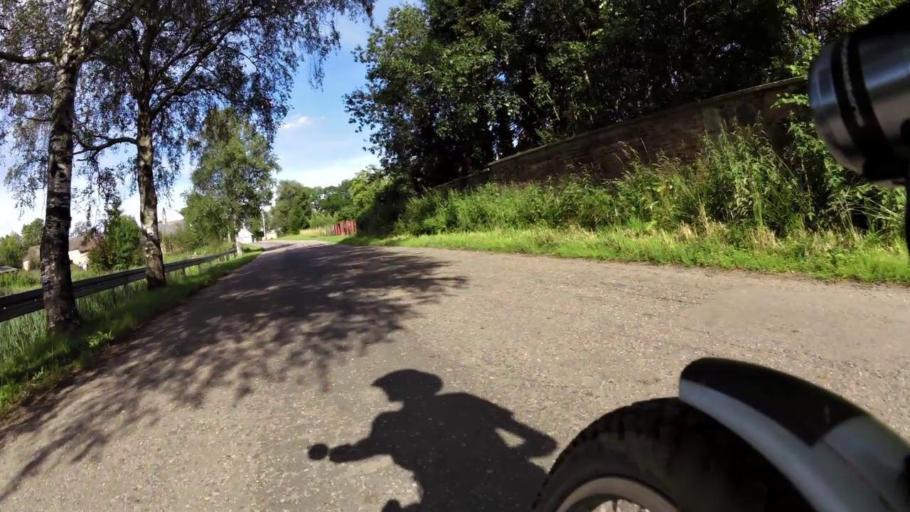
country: PL
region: West Pomeranian Voivodeship
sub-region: Powiat lobeski
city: Radowo Male
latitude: 53.5820
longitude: 15.4622
